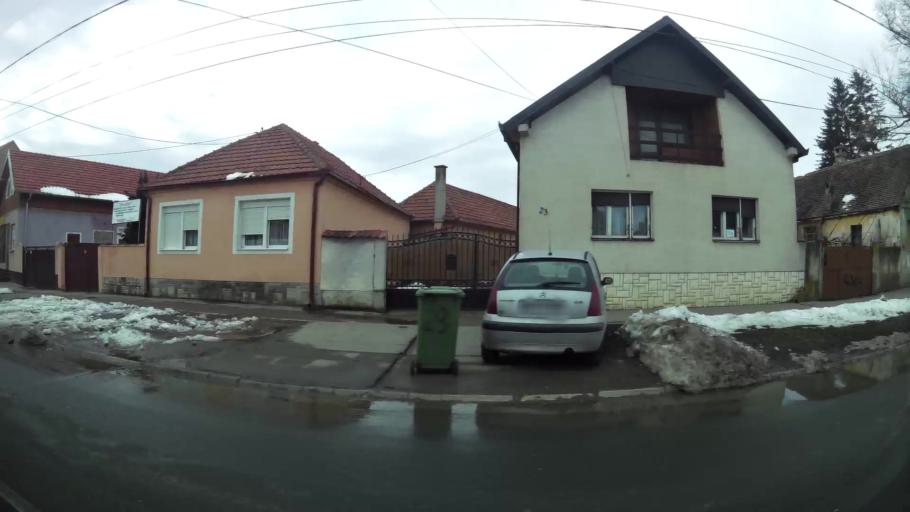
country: RS
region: Central Serbia
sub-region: Belgrade
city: Surcin
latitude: 44.7929
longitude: 20.2689
